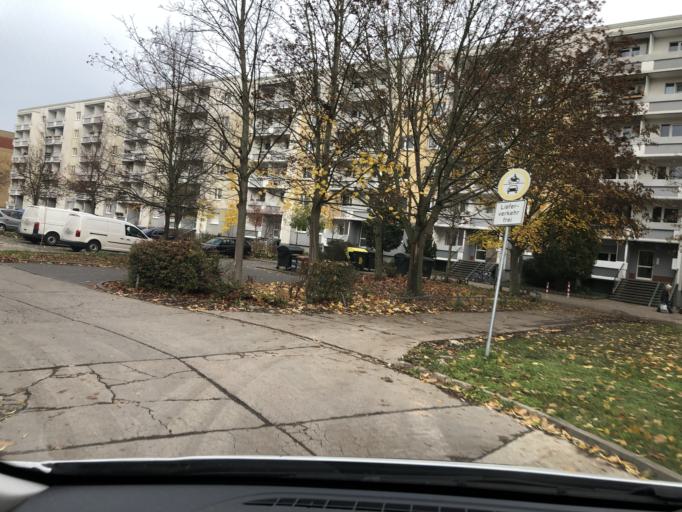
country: DE
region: Saxony-Anhalt
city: Halle Neustadt
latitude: 51.4683
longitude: 11.9260
